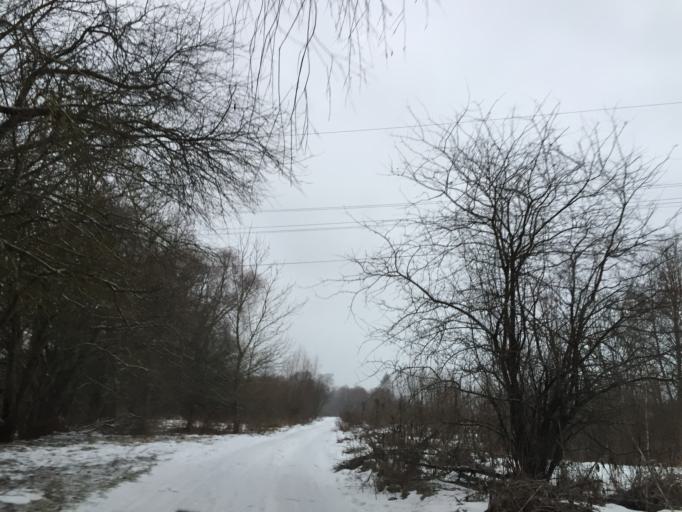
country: LV
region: Riga
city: Riga
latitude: 56.9198
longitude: 24.1350
